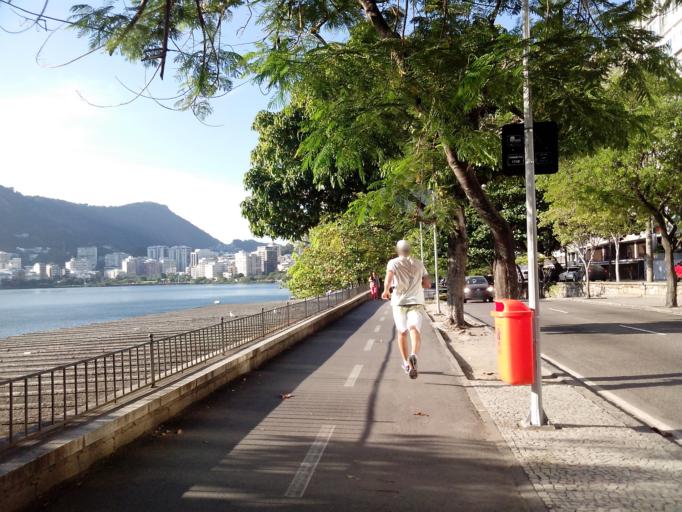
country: BR
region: Rio de Janeiro
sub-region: Rio De Janeiro
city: Rio de Janeiro
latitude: -22.9719
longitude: -43.2080
